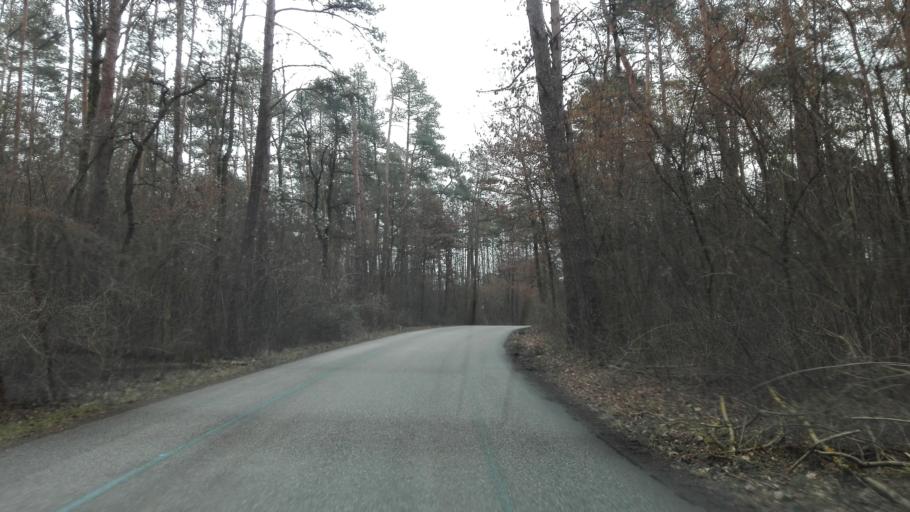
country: AT
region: Upper Austria
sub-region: Politischer Bezirk Linz-Land
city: Traun
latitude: 48.2375
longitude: 14.2237
